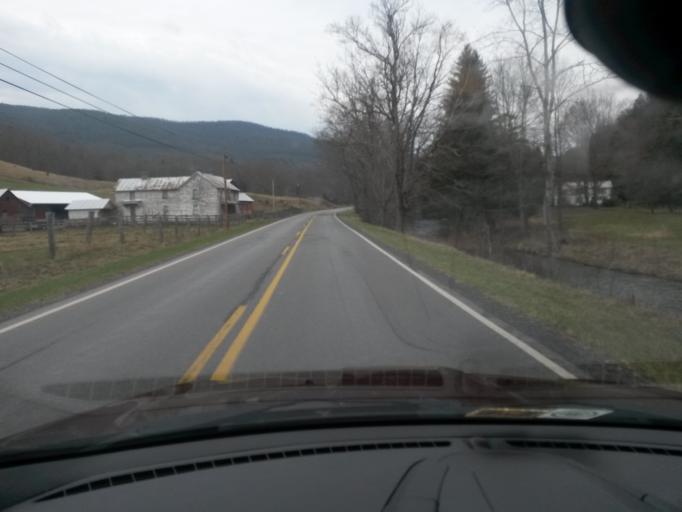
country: US
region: Virginia
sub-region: Highland County
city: Monterey
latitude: 38.3399
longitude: -79.6336
